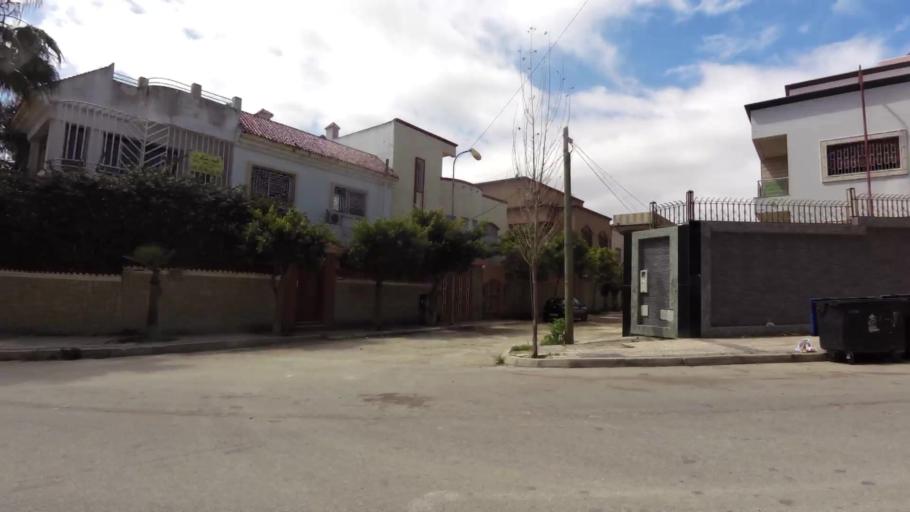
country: MA
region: Tanger-Tetouan
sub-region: Tanger-Assilah
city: Tangier
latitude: 35.7645
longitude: -5.8396
